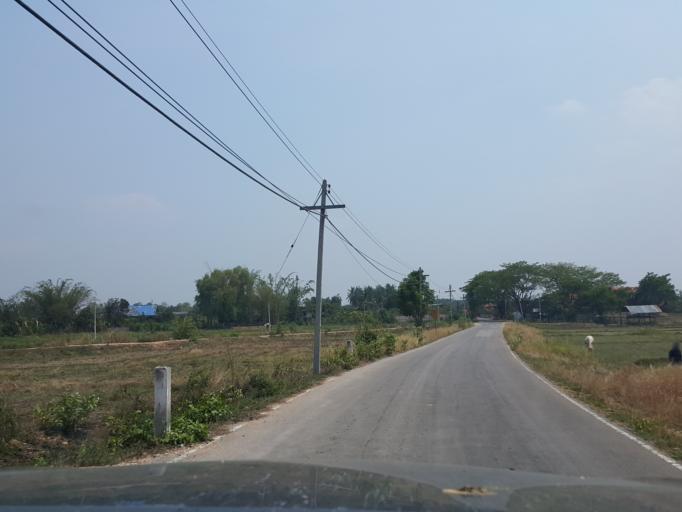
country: TH
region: Lampang
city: Mae Phrik
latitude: 17.5178
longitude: 99.1473
